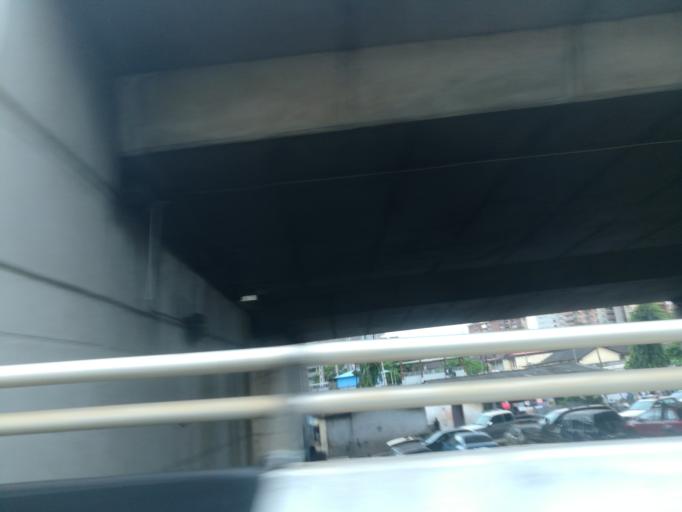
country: NG
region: Lagos
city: Lagos
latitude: 6.4434
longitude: 3.4059
